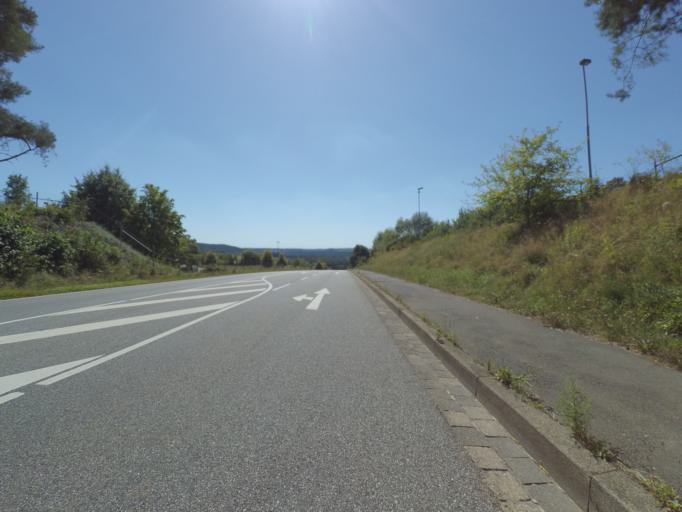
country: DE
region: Rheinland-Pfalz
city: Ulmen
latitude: 50.2106
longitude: 6.9697
